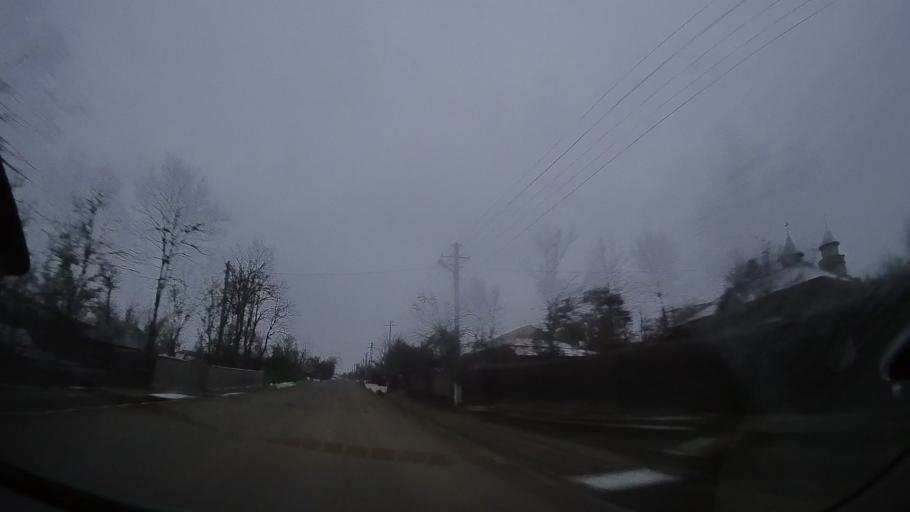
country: RO
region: Vaslui
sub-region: Comuna Gagesti
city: Gagesti
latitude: 46.3899
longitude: 27.9814
